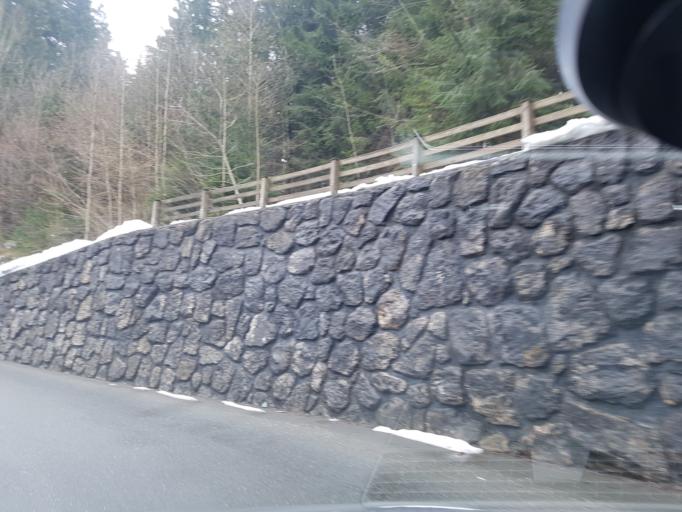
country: AT
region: Tyrol
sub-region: Politischer Bezirk Kufstein
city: Worgl
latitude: 47.4767
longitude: 12.0690
